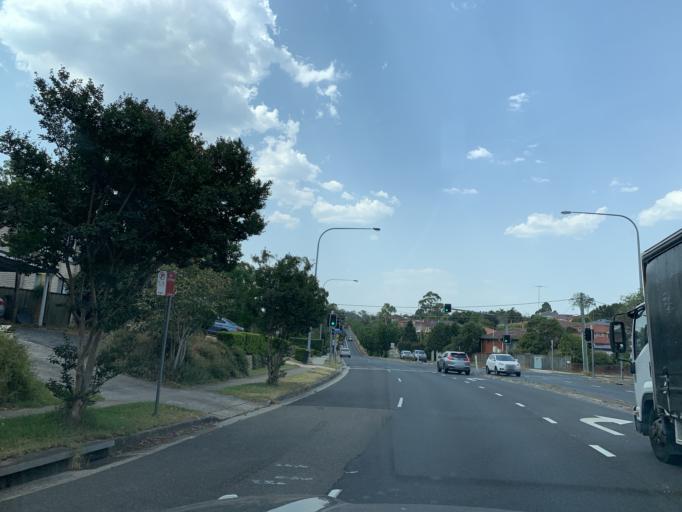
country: AU
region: New South Wales
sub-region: The Hills Shire
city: West Pennant
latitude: -33.7297
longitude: 151.0310
